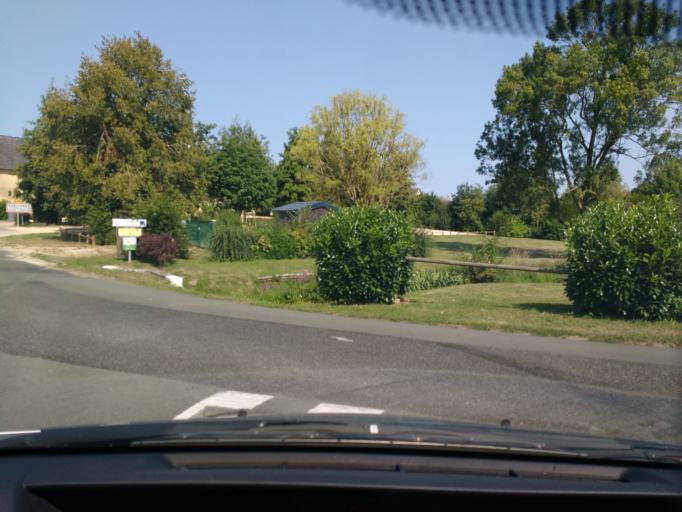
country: FR
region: Pays de la Loire
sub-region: Departement de Maine-et-Loire
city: Bauge-en-Anjou
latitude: 47.5465
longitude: -0.0397
